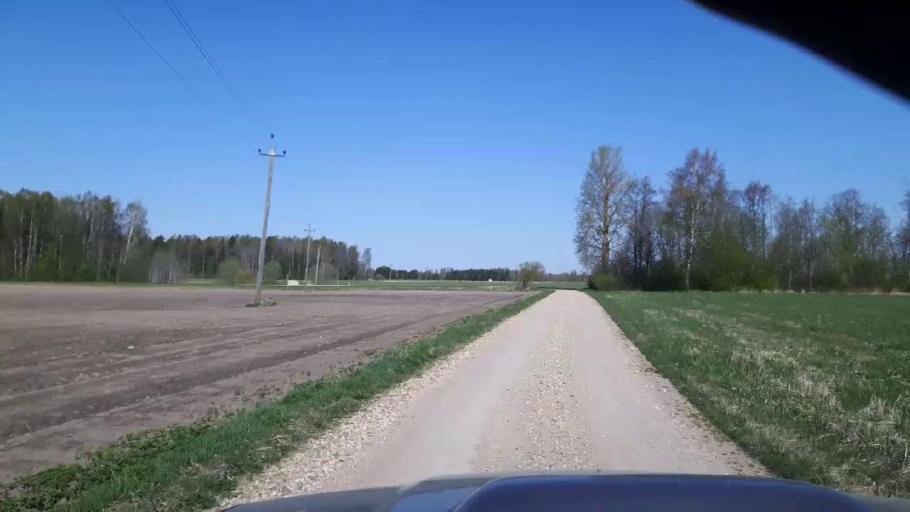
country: EE
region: Paernumaa
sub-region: Sindi linn
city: Sindi
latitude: 58.4522
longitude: 24.7803
